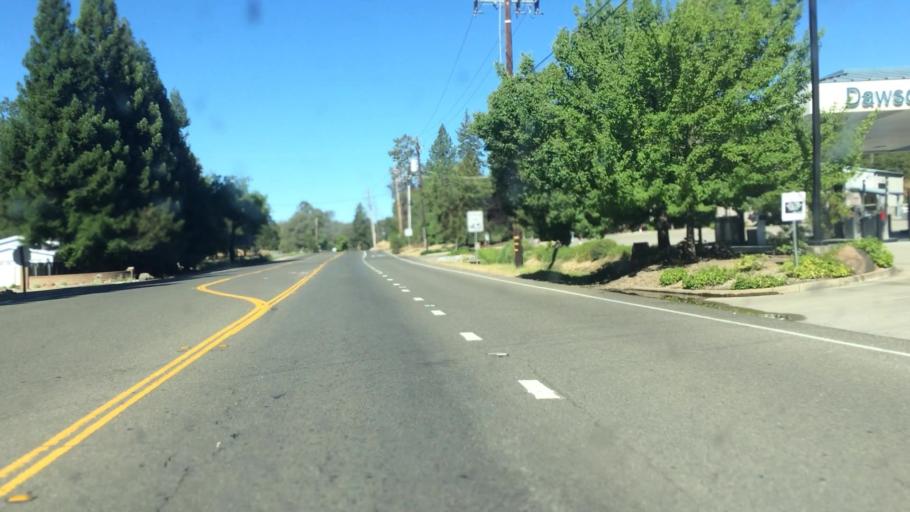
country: US
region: California
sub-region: El Dorado County
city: Diamond Springs
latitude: 38.6928
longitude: -120.8240
